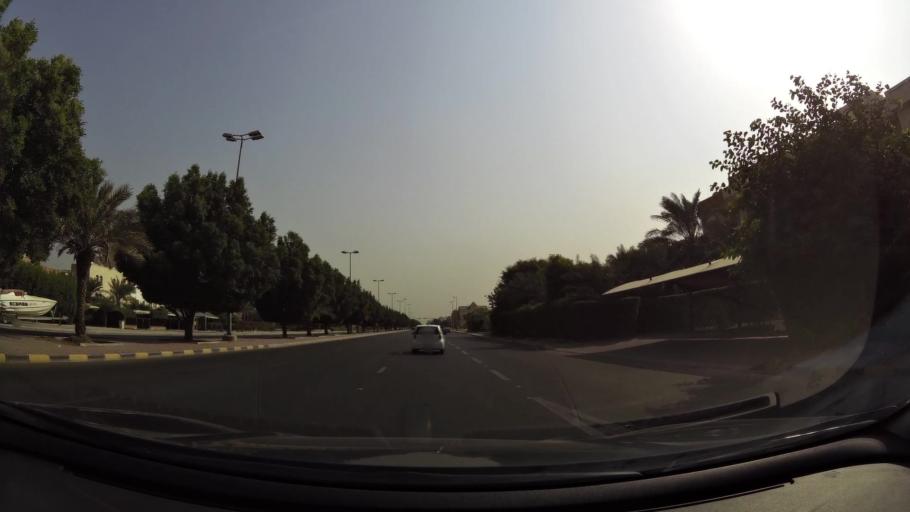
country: KW
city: Bayan
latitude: 29.2871
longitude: 48.0510
